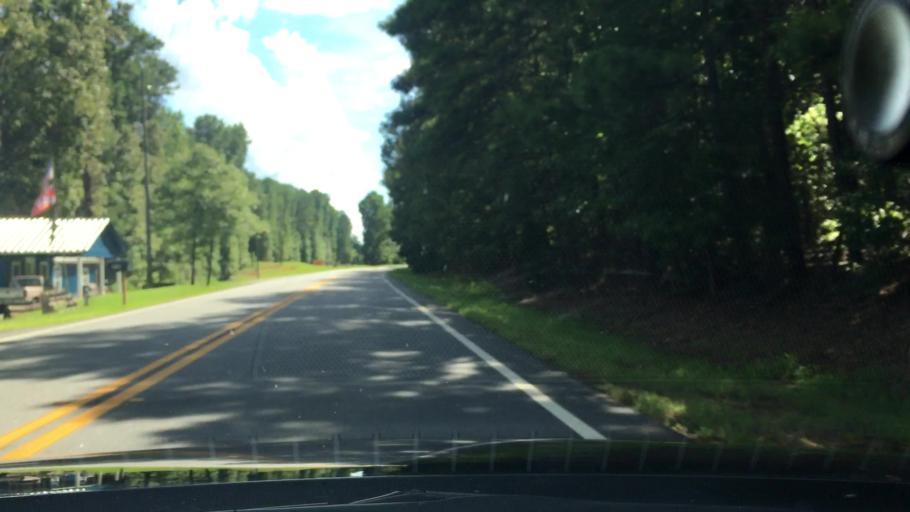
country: US
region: Georgia
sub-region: Butts County
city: Indian Springs
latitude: 33.2921
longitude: -83.8742
